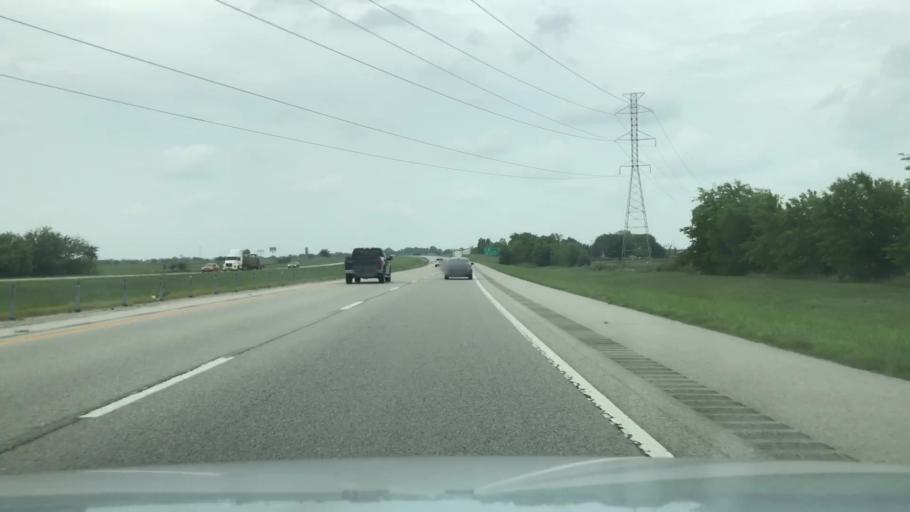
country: US
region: Oklahoma
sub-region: Osage County
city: Skiatook
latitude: 36.3447
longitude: -95.9227
